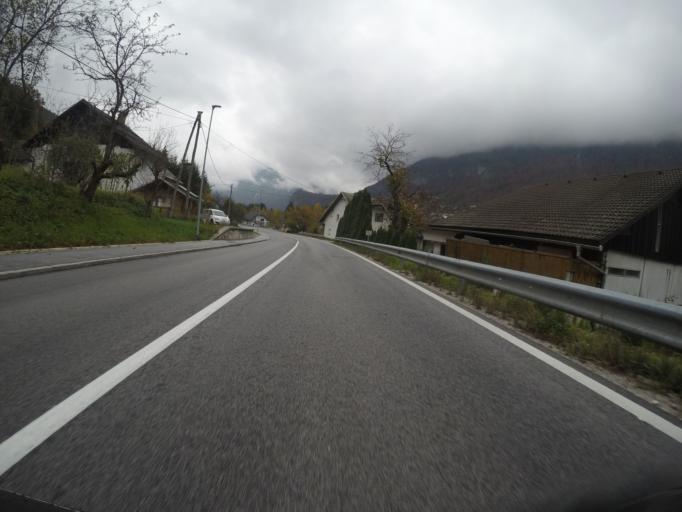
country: SI
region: Kranjska Gora
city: Mojstrana
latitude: 46.4724
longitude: 13.9149
